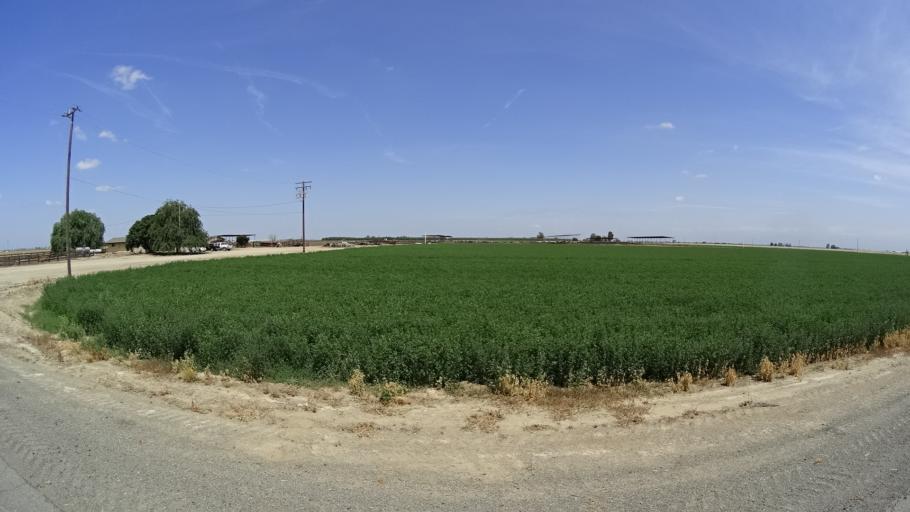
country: US
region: California
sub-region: Tulare County
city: Goshen
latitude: 36.2979
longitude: -119.4784
